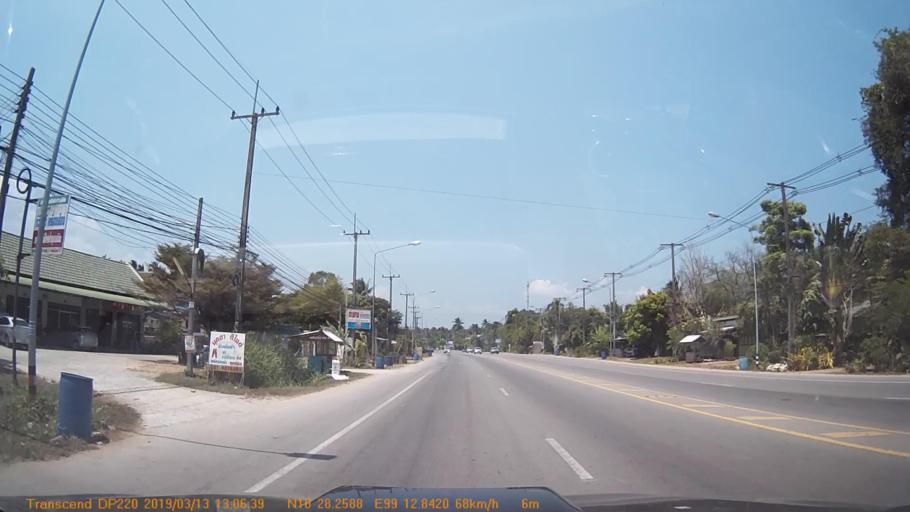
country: TH
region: Chumphon
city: Chumphon
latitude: 10.4713
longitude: 99.2139
